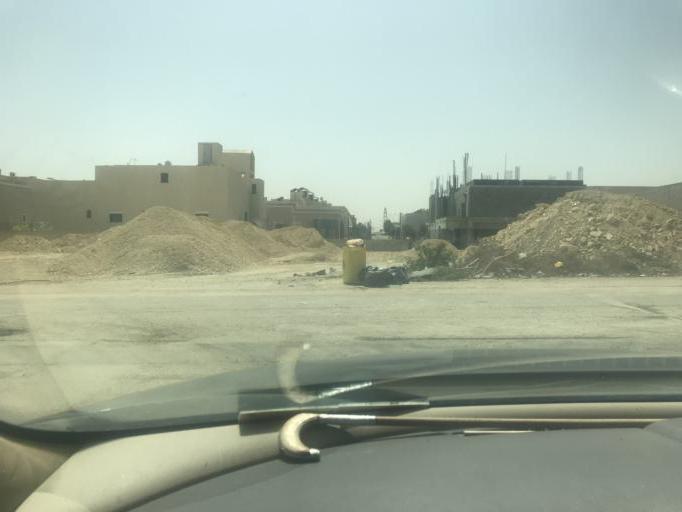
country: SA
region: Ar Riyad
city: Riyadh
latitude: 24.7856
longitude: 46.5828
